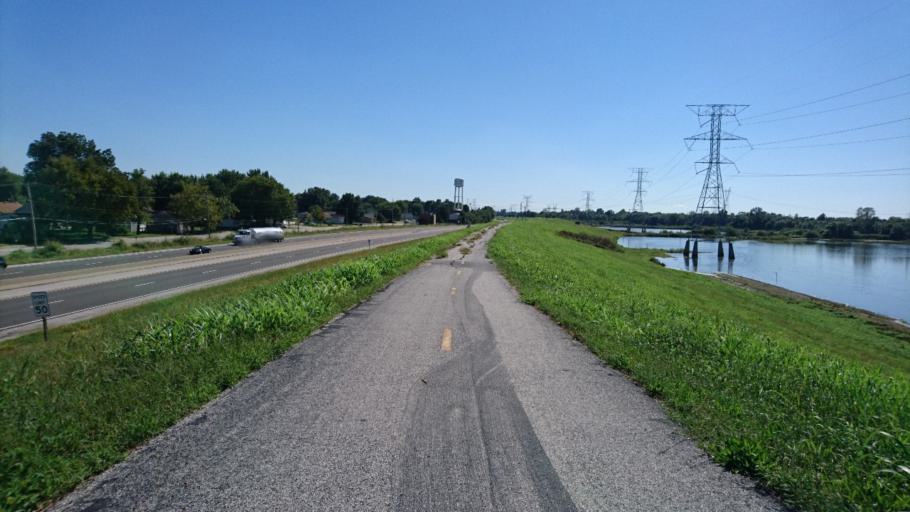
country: US
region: Illinois
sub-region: Madison County
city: Hartford
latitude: 38.8370
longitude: -90.0984
